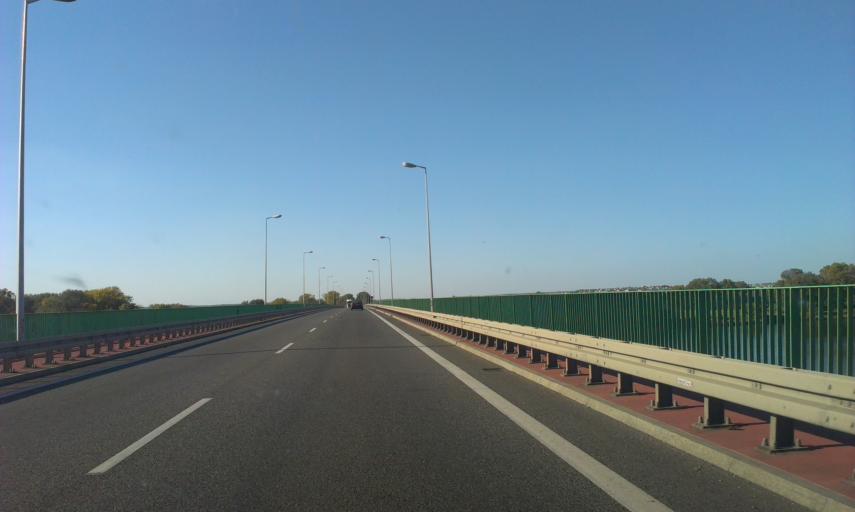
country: PL
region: Kujawsko-Pomorskie
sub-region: Powiat chelminski
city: Chelmno
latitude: 53.3680
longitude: 18.4297
